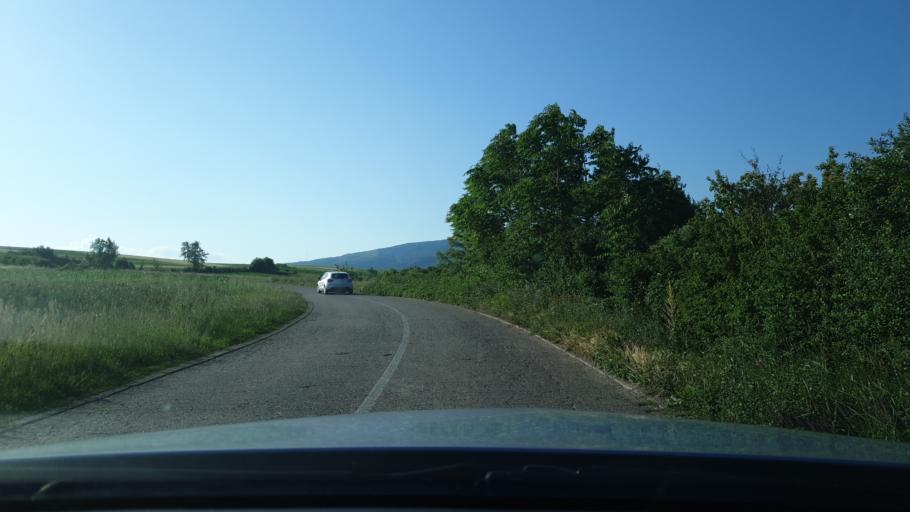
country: RS
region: Central Serbia
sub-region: Nisavski Okrug
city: Aleksinac
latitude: 43.6178
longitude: 21.6823
